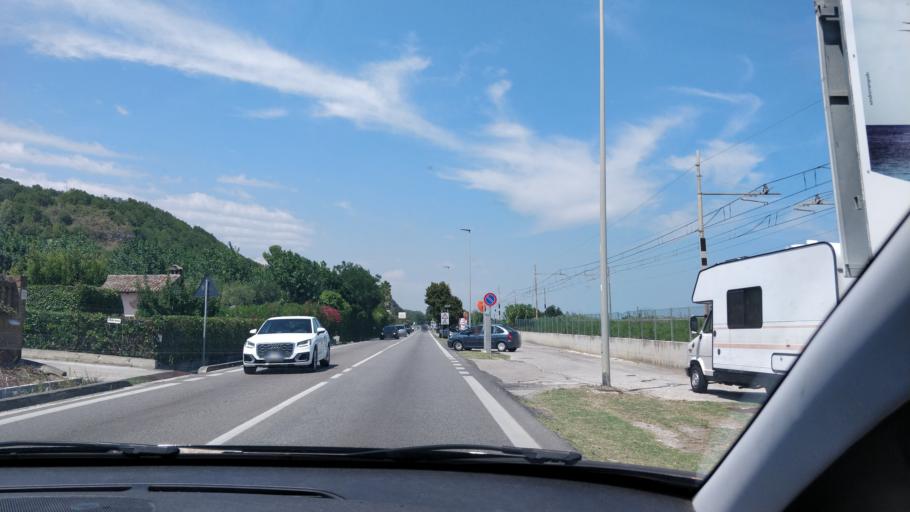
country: IT
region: Abruzzo
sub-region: Provincia di Chieti
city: Tollo
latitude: 42.3814
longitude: 14.3639
